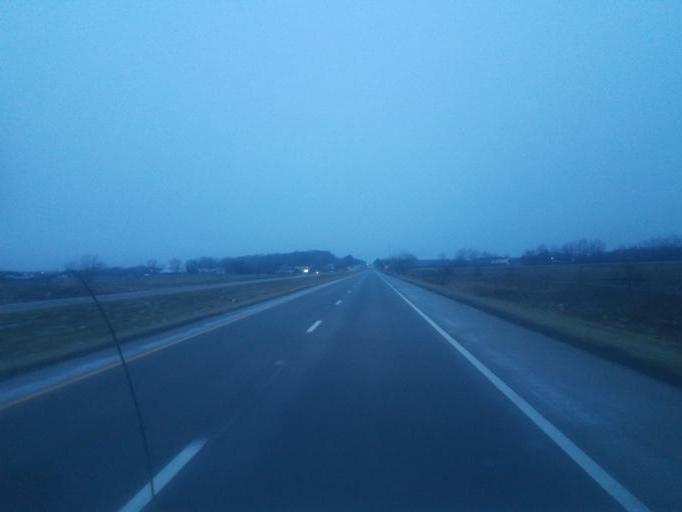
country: US
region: Ohio
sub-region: Ashland County
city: Ashland
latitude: 40.7854
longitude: -82.1912
